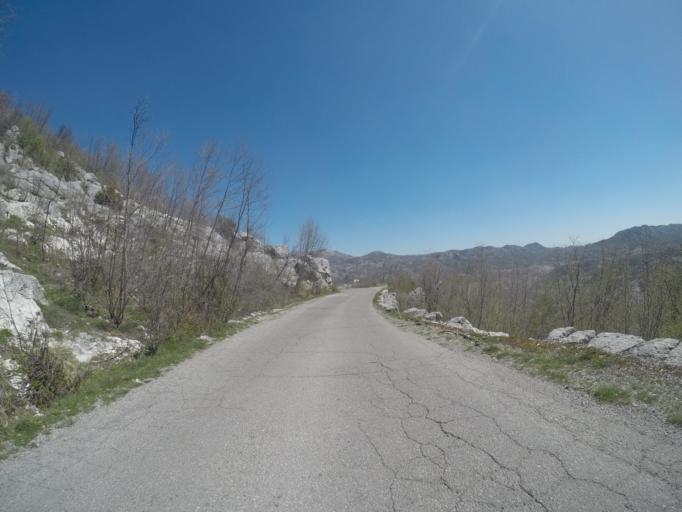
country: ME
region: Cetinje
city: Cetinje
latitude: 42.4367
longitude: 18.8698
